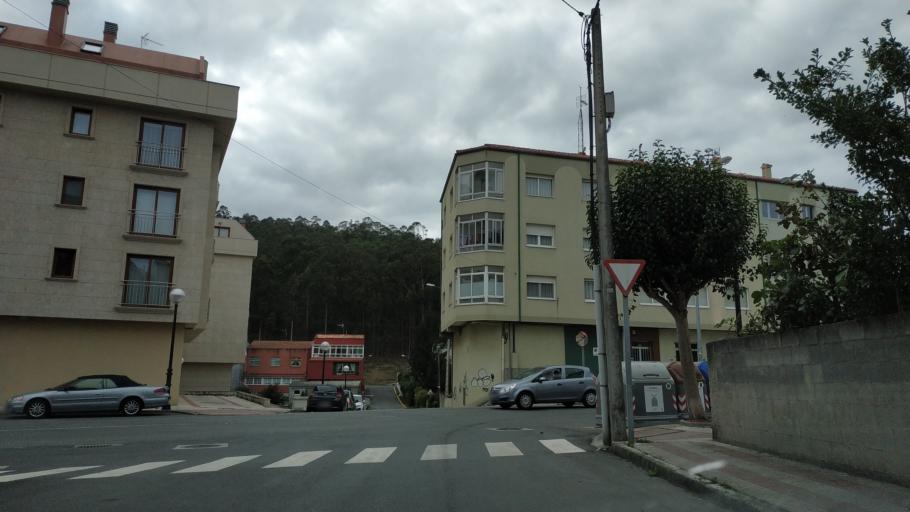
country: ES
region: Galicia
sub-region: Provincia da Coruna
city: Arteixo
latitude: 43.3016
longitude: -8.5116
